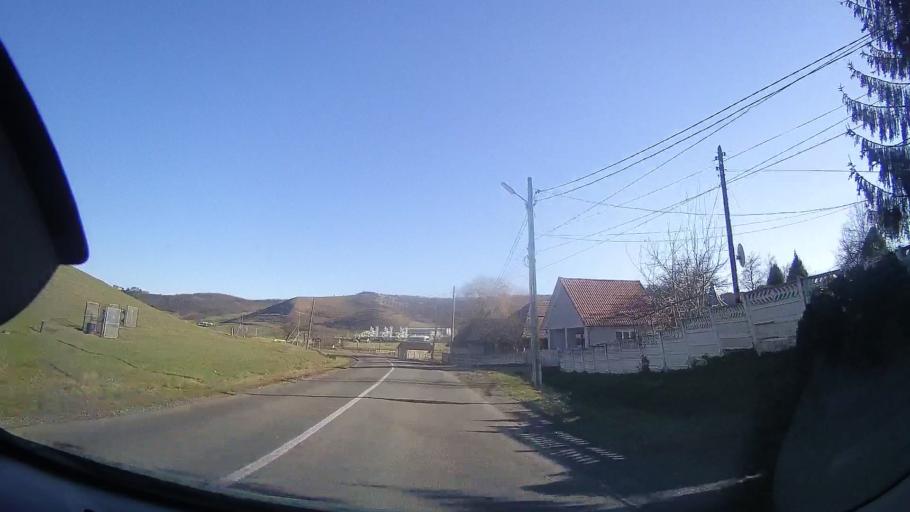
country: RO
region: Mures
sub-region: Comuna Sarmasu
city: Sarmasu
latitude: 46.7718
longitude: 24.1939
